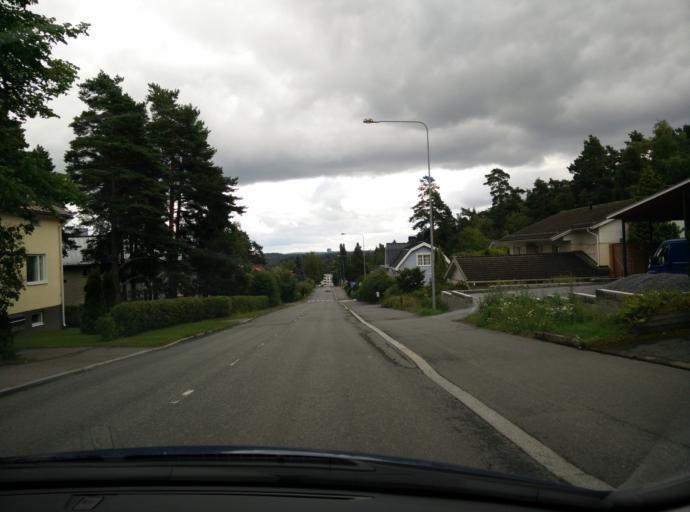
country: FI
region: Haeme
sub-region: Haemeenlinna
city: Haemeenlinna
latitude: 60.9868
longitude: 24.4505
